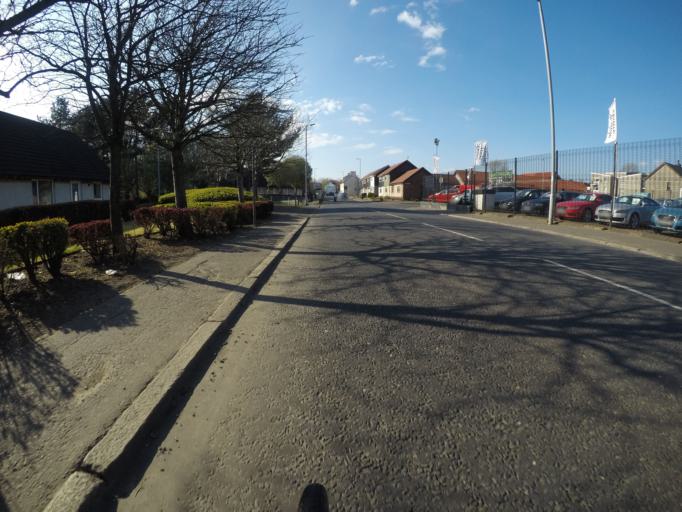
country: GB
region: Scotland
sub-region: North Ayrshire
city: Kilwinning
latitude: 55.6533
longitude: -4.6926
